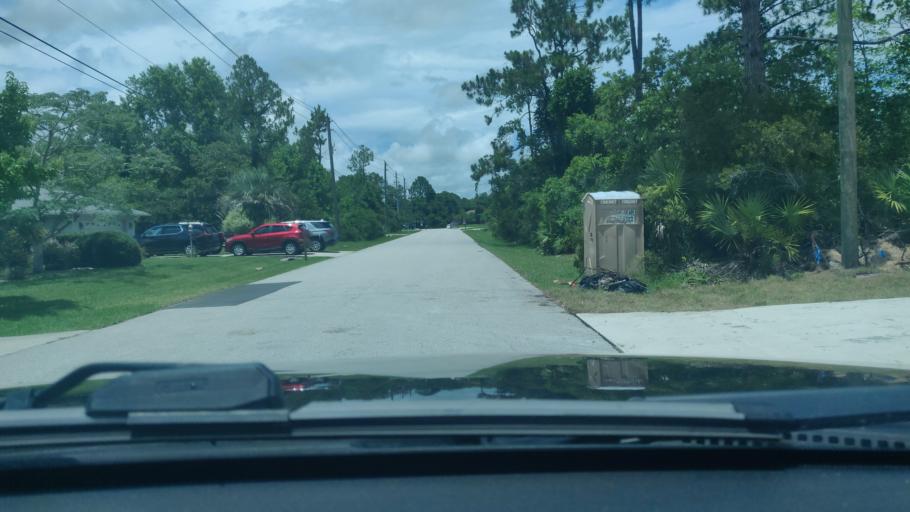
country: US
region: Florida
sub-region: Flagler County
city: Bunnell
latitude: 29.5210
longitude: -81.2564
